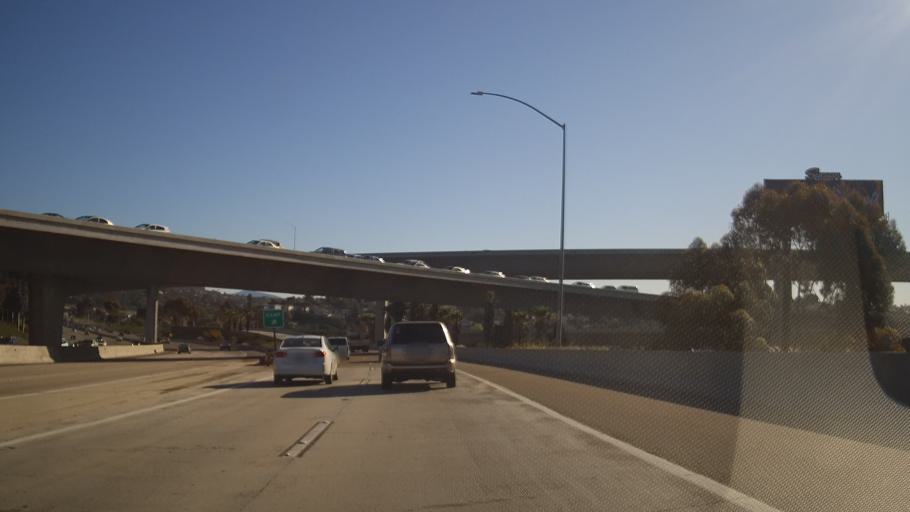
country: US
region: California
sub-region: San Diego County
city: Lemon Grove
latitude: 32.7454
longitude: -117.0198
